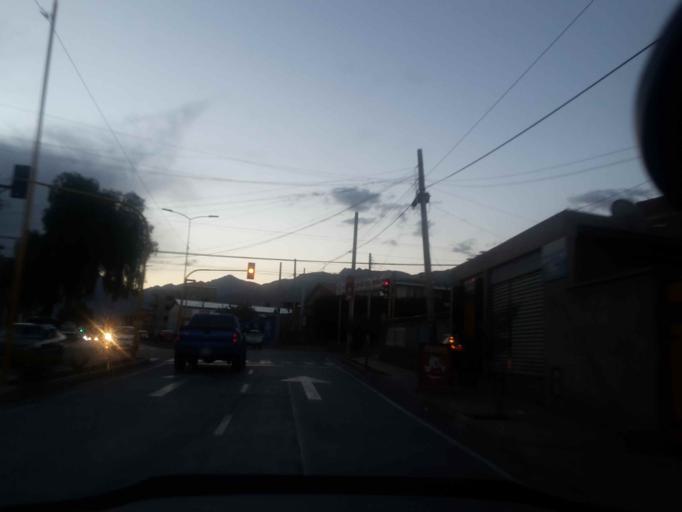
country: BO
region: Cochabamba
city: Cochabamba
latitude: -17.3483
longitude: -66.1910
